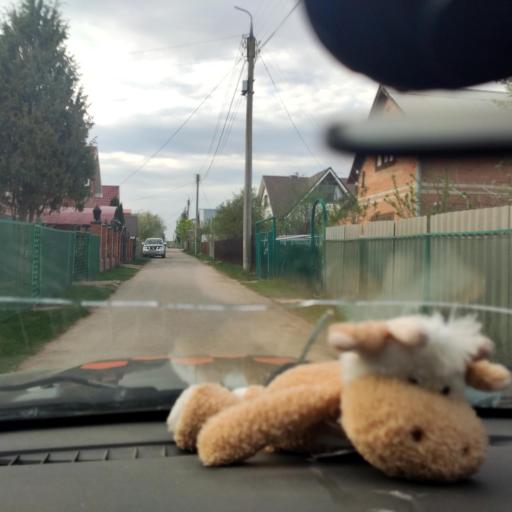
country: RU
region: Samara
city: Podstepki
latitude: 53.5073
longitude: 49.1901
